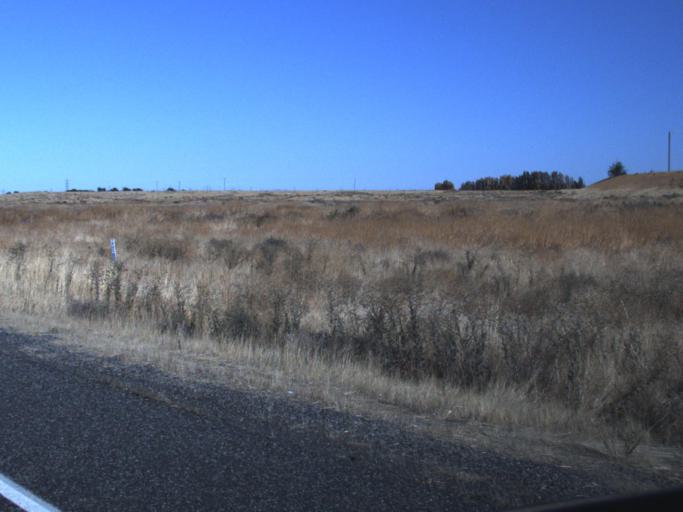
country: US
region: Washington
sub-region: Benton County
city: West Richland
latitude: 46.3438
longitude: -119.3503
